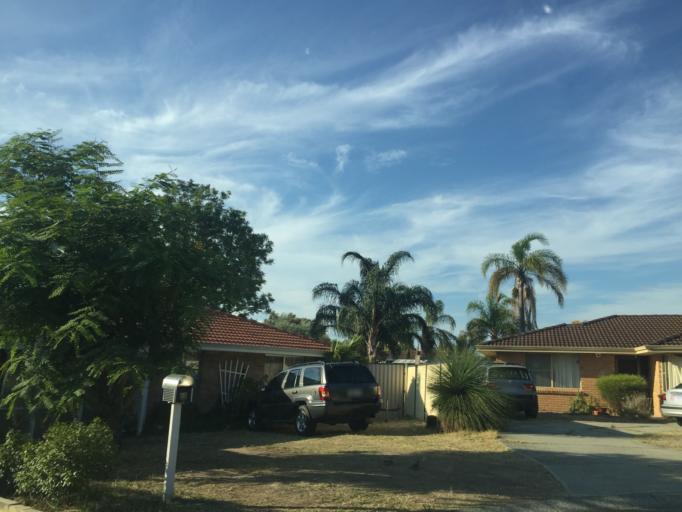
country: AU
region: Western Australia
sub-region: City of Cockburn
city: City of Cockburn
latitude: -32.0922
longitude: 115.8410
